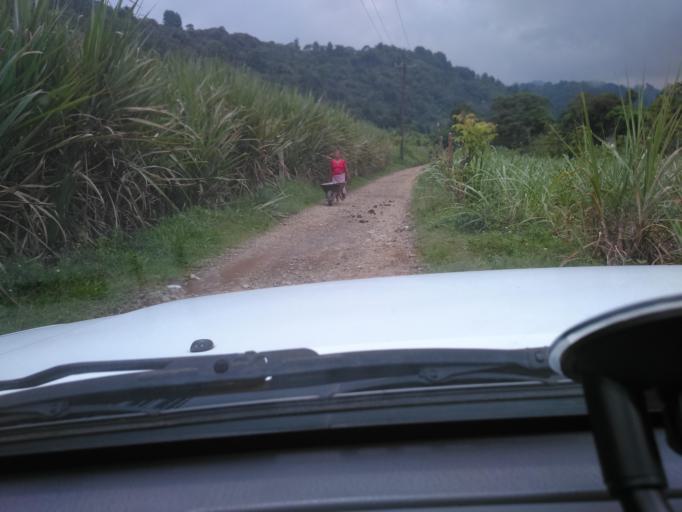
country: MX
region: Veracruz
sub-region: Mariano Escobedo
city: Chicola
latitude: 18.9116
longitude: -97.1120
